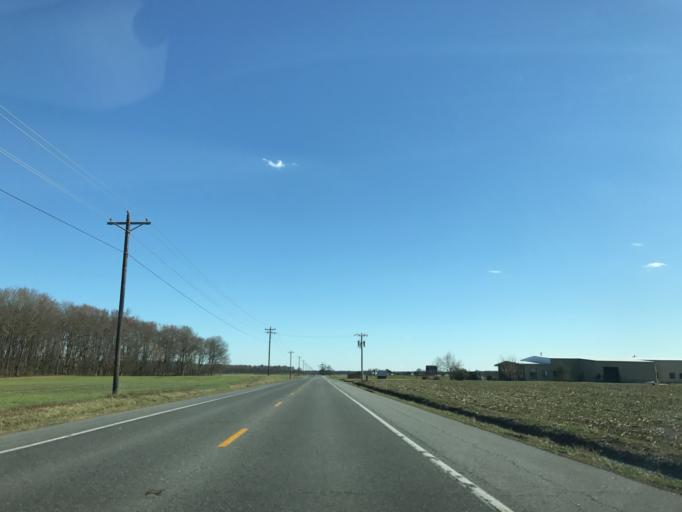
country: US
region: Maryland
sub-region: Caroline County
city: Greensboro
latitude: 39.0867
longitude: -75.8656
